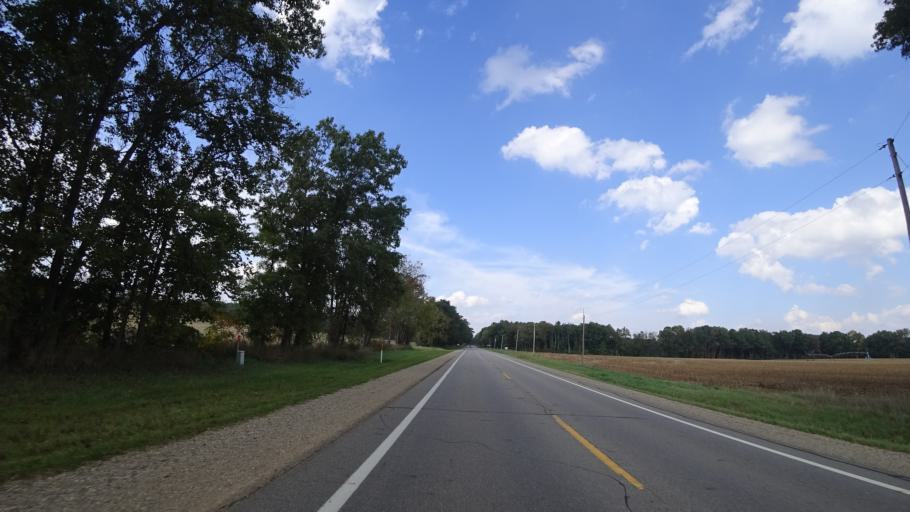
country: US
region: Michigan
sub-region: Saint Joseph County
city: Centreville
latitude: 41.9731
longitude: -85.5670
